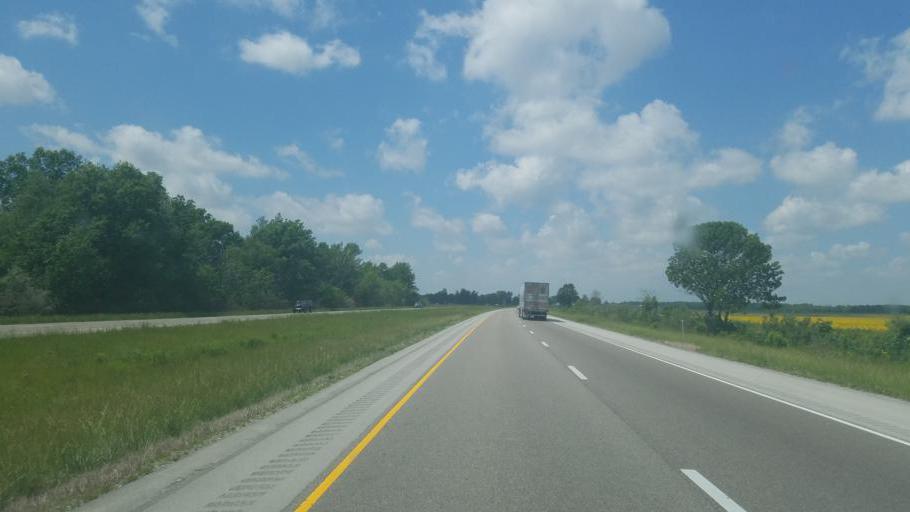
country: US
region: Illinois
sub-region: Cumberland County
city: Greenup
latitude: 39.2384
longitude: -88.1991
